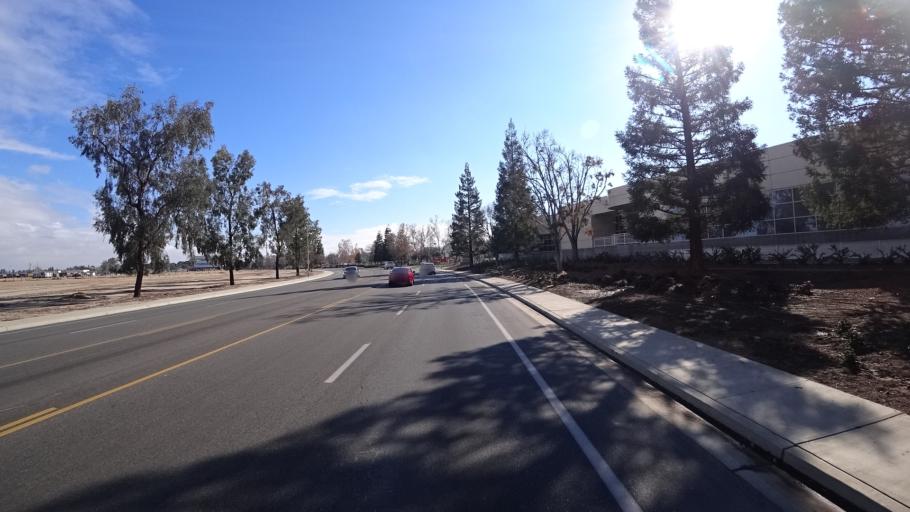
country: US
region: California
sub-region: Kern County
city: Greenacres
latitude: 35.3434
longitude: -119.1118
